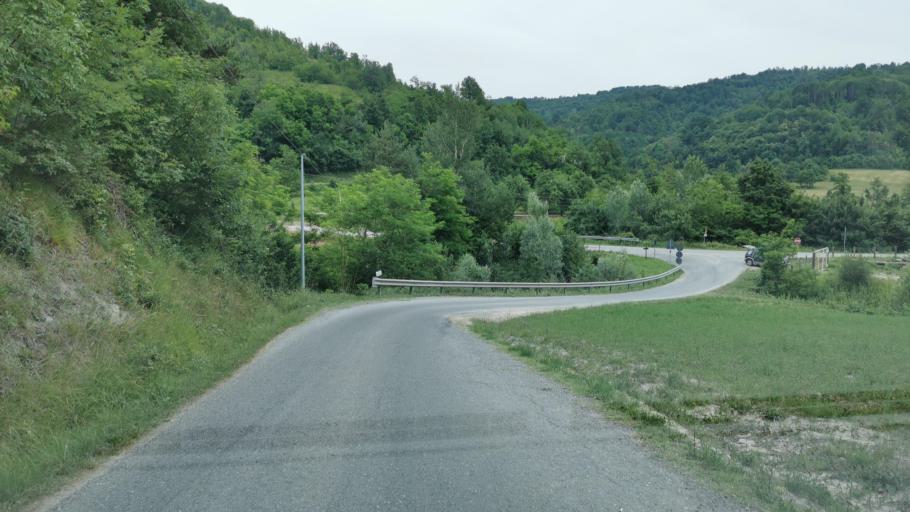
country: IT
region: Piedmont
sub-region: Provincia di Cuneo
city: Paroldo
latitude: 44.4276
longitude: 8.0571
